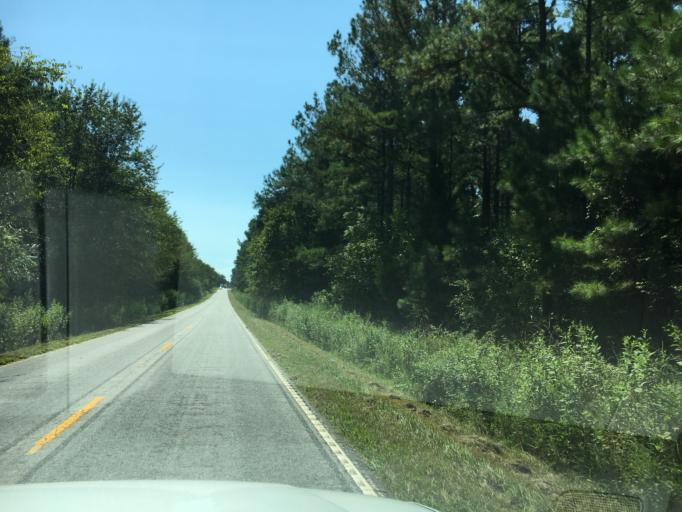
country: US
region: South Carolina
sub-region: Laurens County
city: Joanna
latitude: 34.4148
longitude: -81.8659
